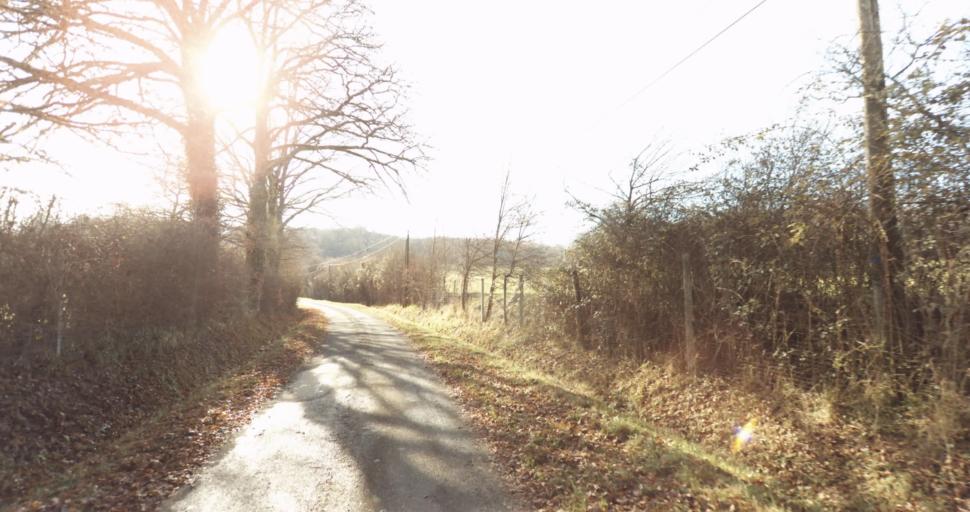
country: FR
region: Limousin
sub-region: Departement de la Haute-Vienne
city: Aixe-sur-Vienne
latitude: 45.7819
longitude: 1.1282
